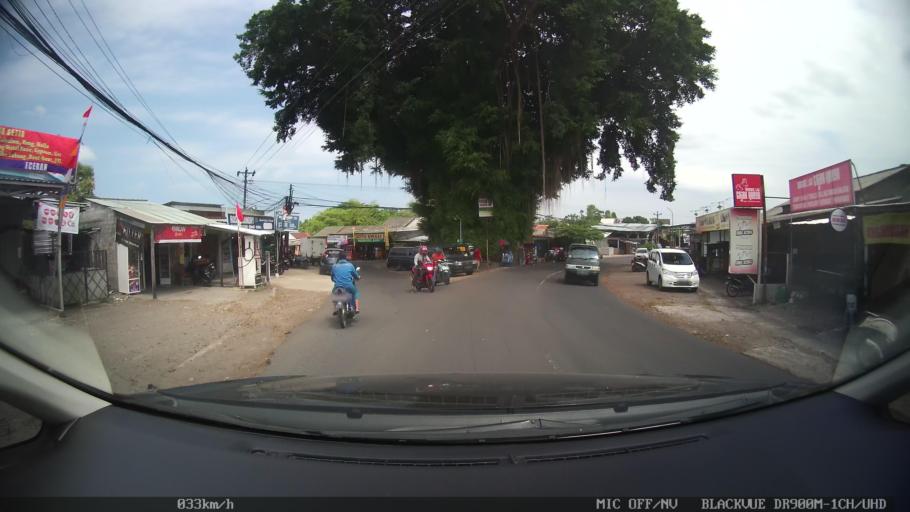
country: ID
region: Daerah Istimewa Yogyakarta
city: Depok
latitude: -7.7391
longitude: 110.4521
